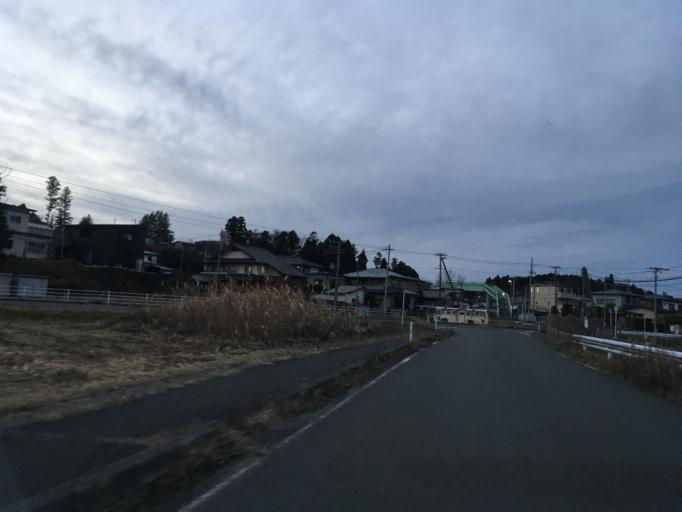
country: JP
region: Miyagi
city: Kogota
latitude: 38.6515
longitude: 141.0759
